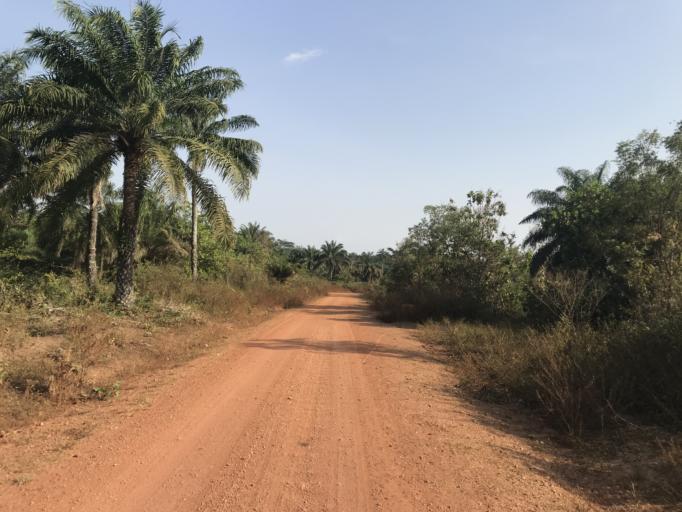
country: NG
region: Osun
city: Inisa
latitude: 7.7828
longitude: 4.3015
